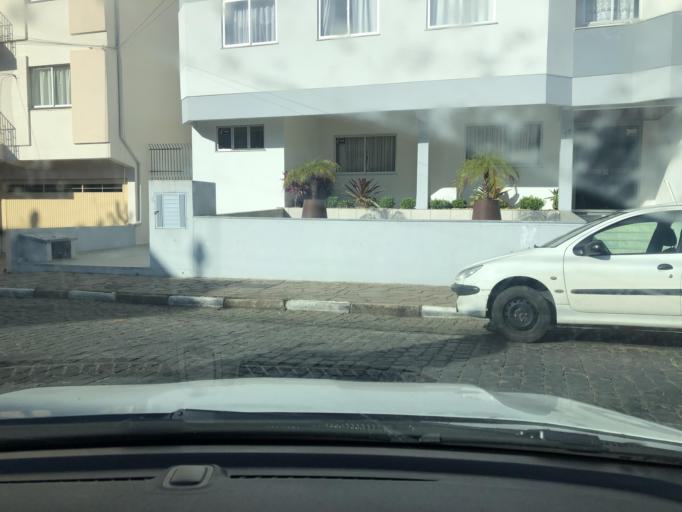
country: BR
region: Santa Catarina
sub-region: Lages
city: Lages
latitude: -27.8120
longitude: -50.3212
